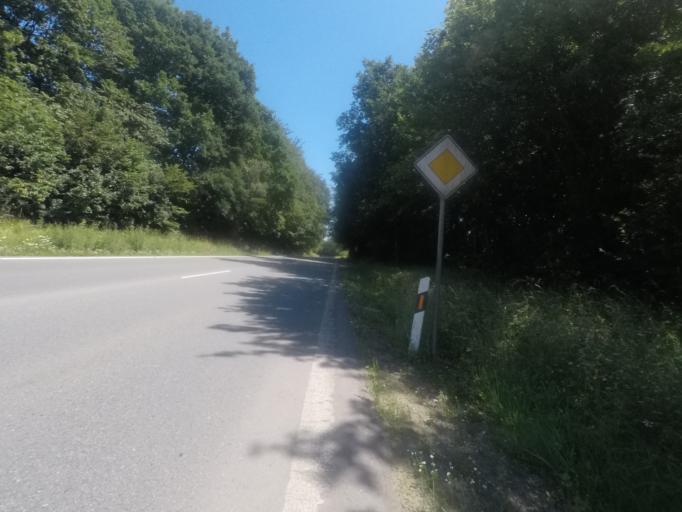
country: DE
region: North Rhine-Westphalia
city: Enger
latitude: 52.0996
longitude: 8.5642
